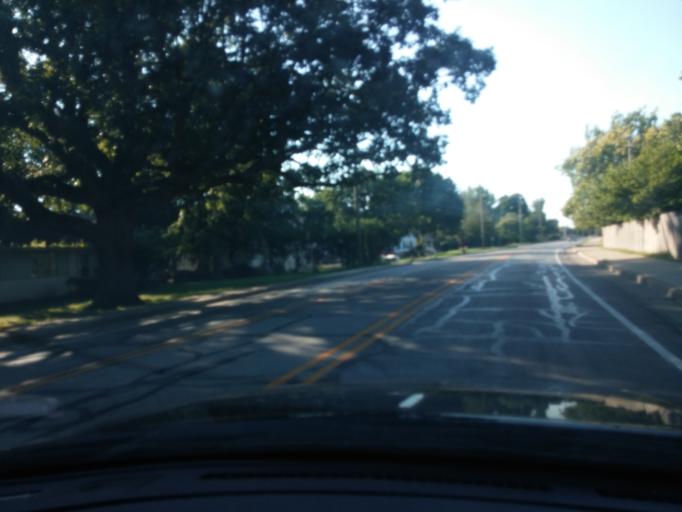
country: US
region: Indiana
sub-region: Tippecanoe County
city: West Lafayette
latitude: 40.4433
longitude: -86.9128
